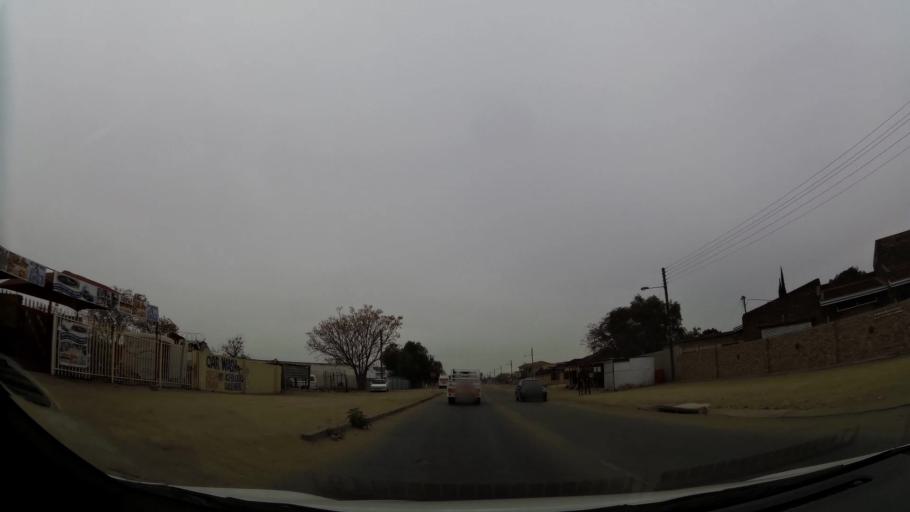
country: ZA
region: Limpopo
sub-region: Capricorn District Municipality
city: Polokwane
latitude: -23.8344
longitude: 29.3873
